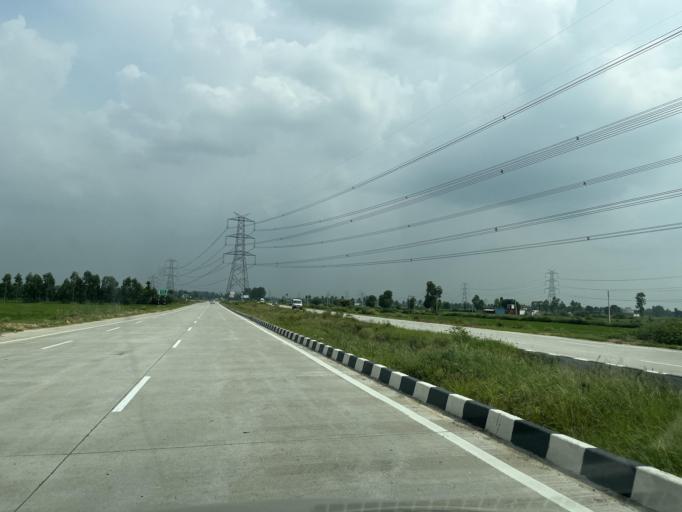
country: IN
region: Uttarakhand
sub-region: Udham Singh Nagar
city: Jaspur
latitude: 29.2859
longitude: 78.8566
